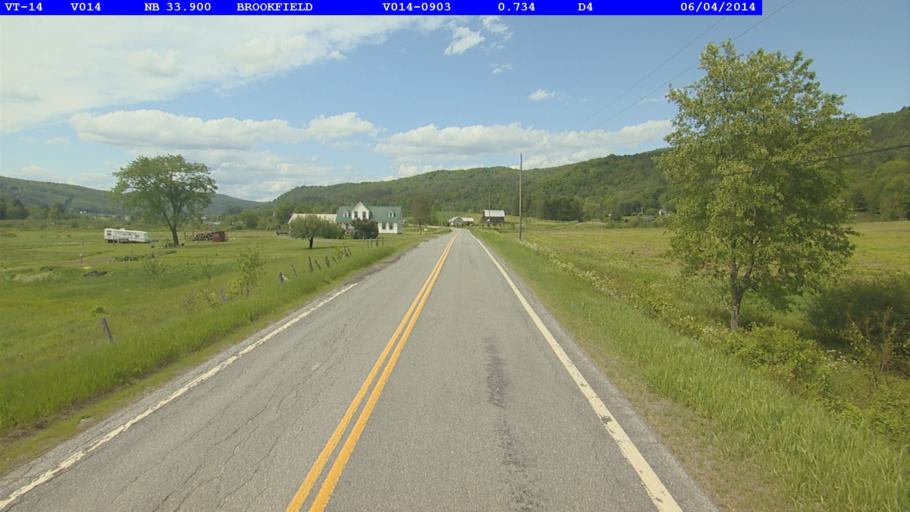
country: US
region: Vermont
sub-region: Orange County
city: Chelsea
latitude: 43.9896
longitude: -72.5561
